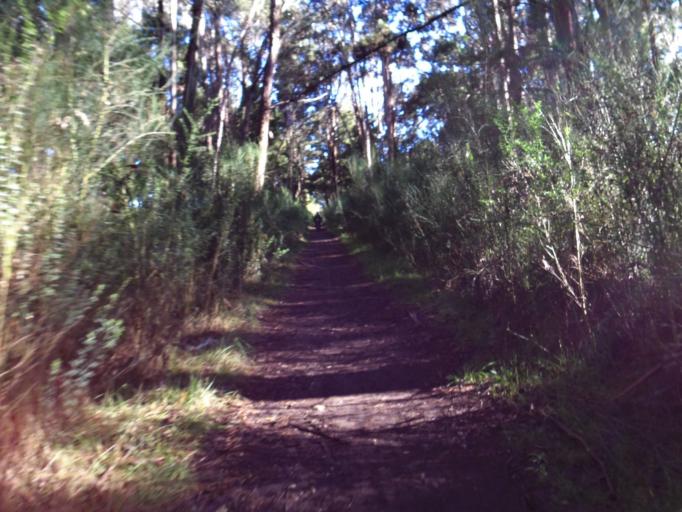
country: AU
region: Victoria
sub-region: Mount Alexander
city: Castlemaine
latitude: -37.3909
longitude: 144.2620
